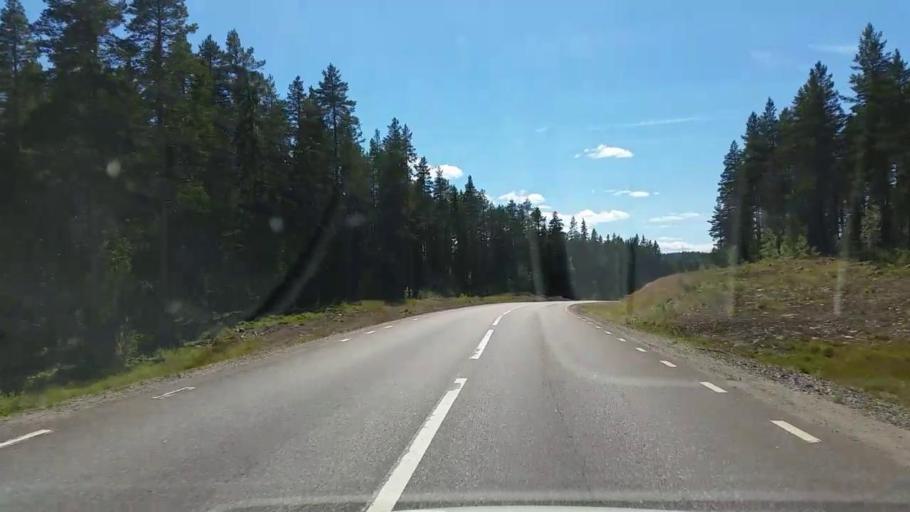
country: SE
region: Gaevleborg
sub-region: Bollnas Kommun
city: Vittsjo
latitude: 61.0917
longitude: 15.8216
